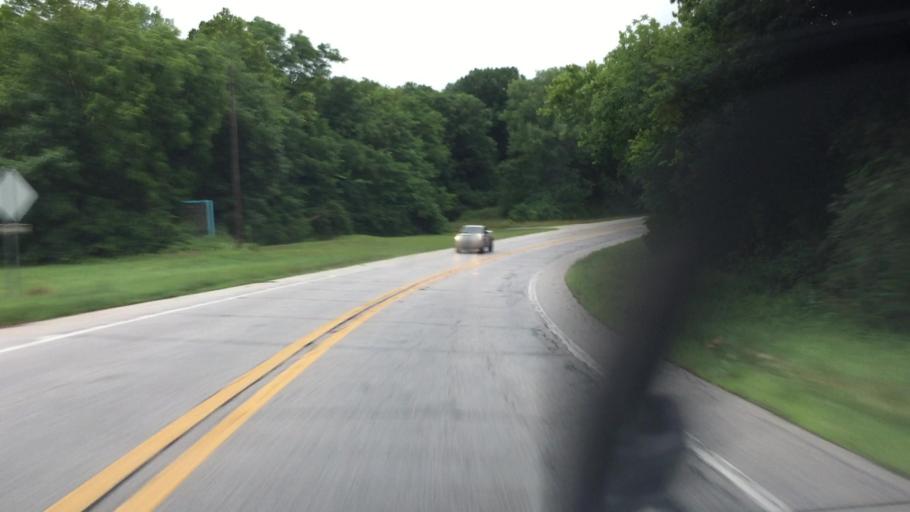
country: US
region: Illinois
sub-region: Hancock County
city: Nauvoo
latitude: 40.5184
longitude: -91.3595
